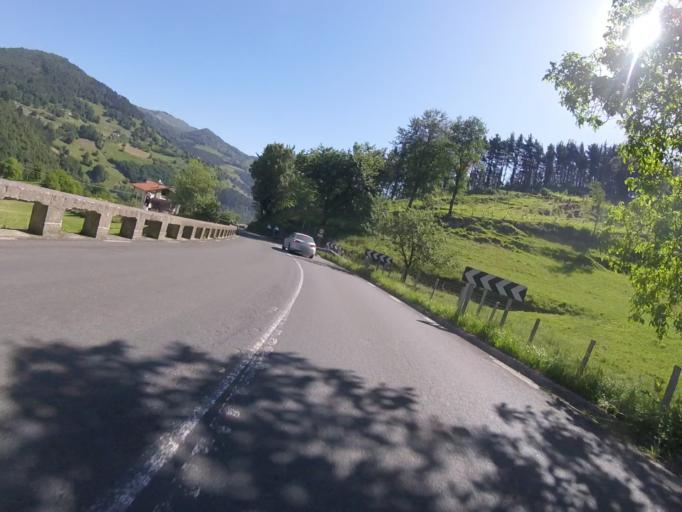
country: ES
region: Basque Country
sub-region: Provincia de Guipuzcoa
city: Albiztur
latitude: 43.1241
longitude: -2.1392
